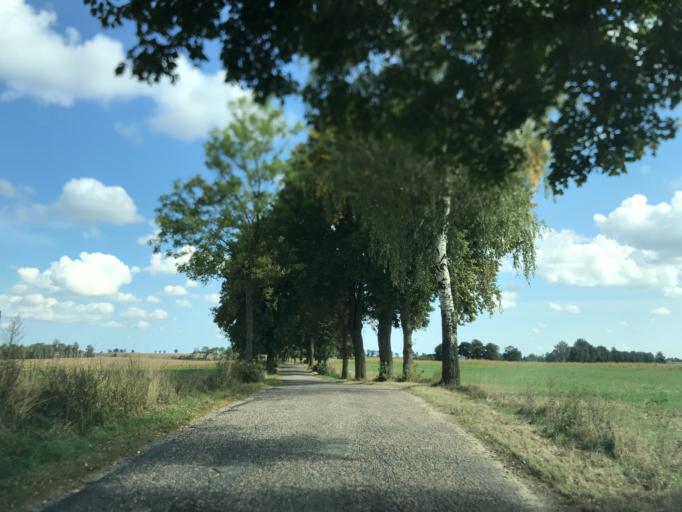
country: PL
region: Kujawsko-Pomorskie
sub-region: Powiat brodnicki
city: Brzozie
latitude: 53.3540
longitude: 19.6720
